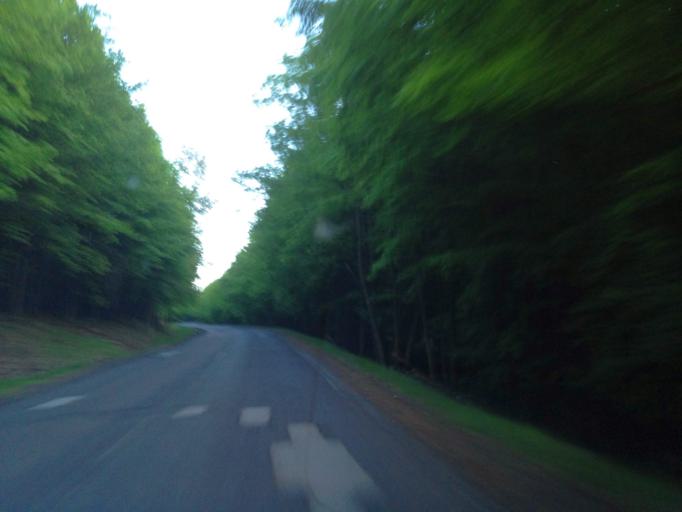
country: HU
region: Nograd
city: Batonyterenye
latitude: 47.8985
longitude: 19.8572
